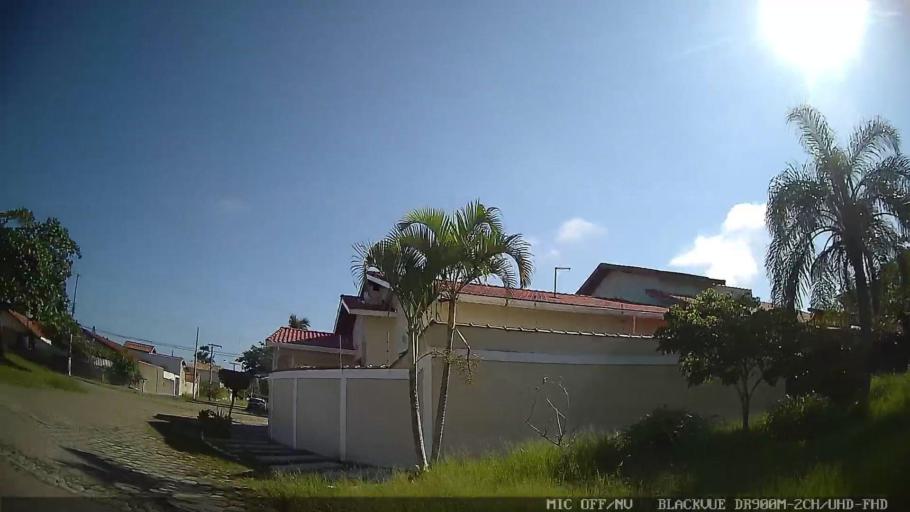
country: BR
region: Sao Paulo
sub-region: Peruibe
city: Peruibe
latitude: -24.2922
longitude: -46.9677
